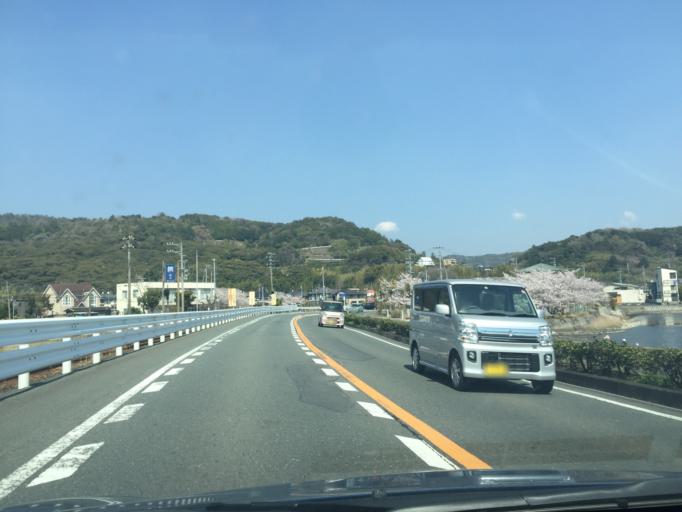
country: JP
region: Shizuoka
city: Kosai-shi
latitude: 34.8004
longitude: 137.6193
